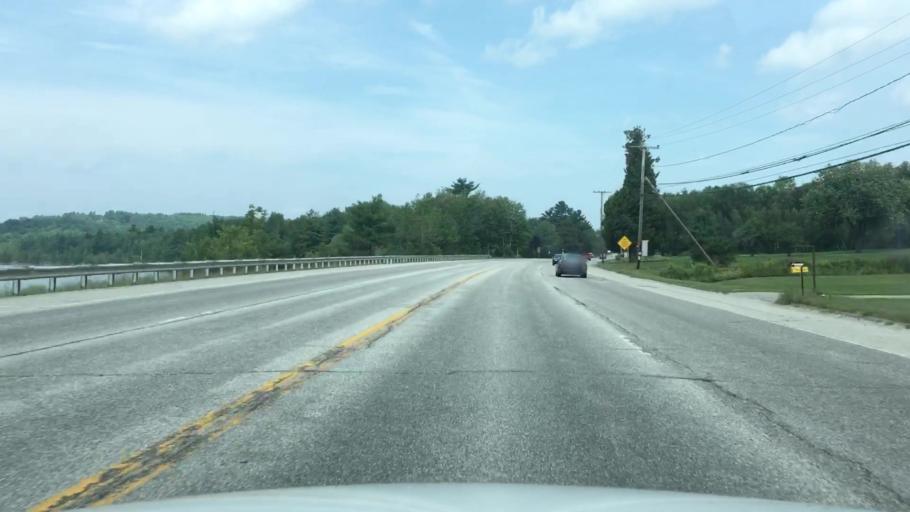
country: US
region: Maine
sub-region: Androscoggin County
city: Auburn
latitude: 44.1532
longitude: -70.2323
